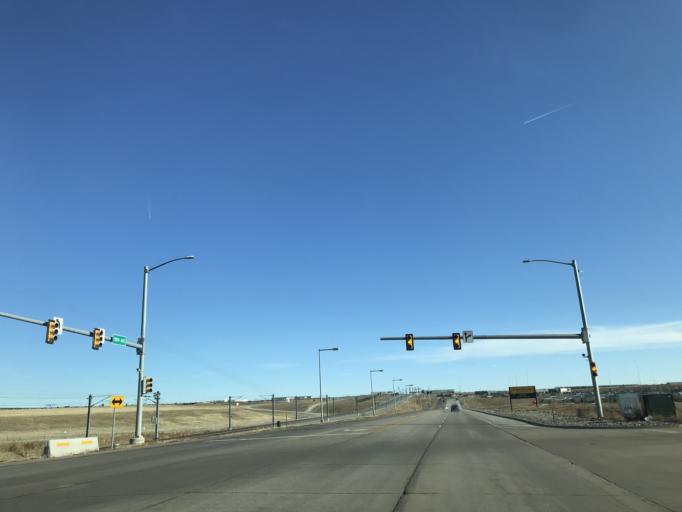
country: US
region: Colorado
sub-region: Weld County
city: Lochbuie
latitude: 39.8379
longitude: -104.6871
